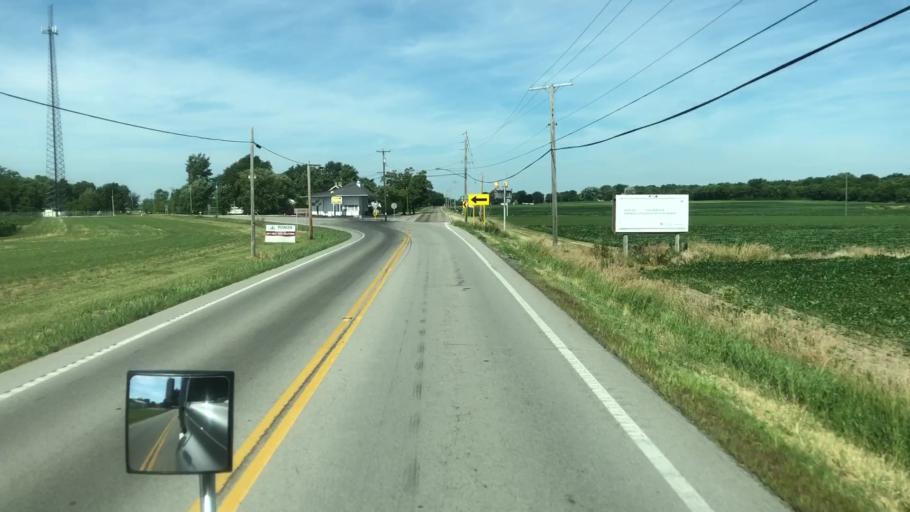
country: US
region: Ohio
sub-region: Erie County
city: Sandusky
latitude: 41.4355
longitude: -82.8317
